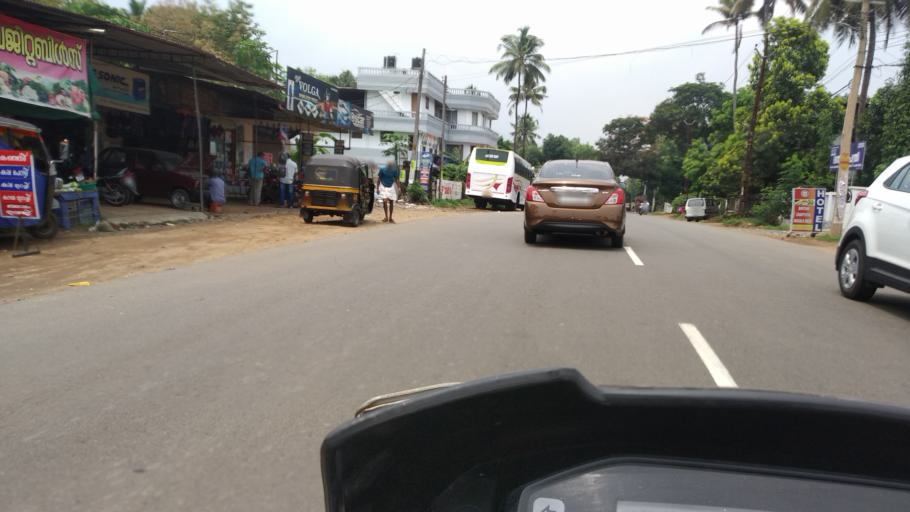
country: IN
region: Kerala
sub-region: Ernakulam
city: Perumpavur
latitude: 10.1160
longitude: 76.4980
